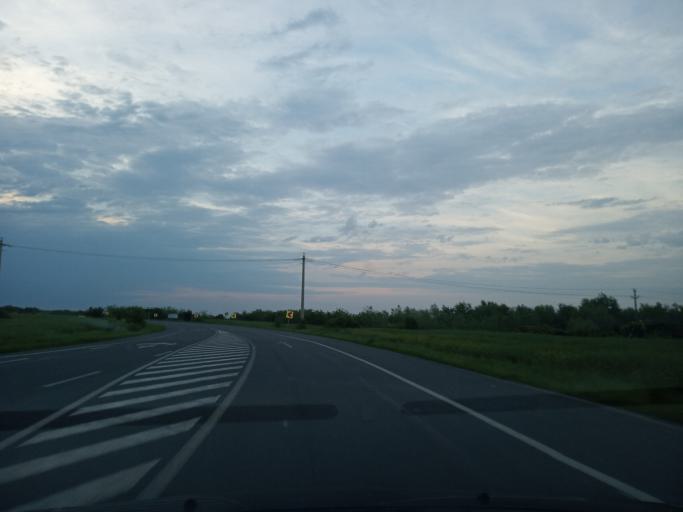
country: RO
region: Timis
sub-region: Oras Deta
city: Deta
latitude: 45.4043
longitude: 21.2382
